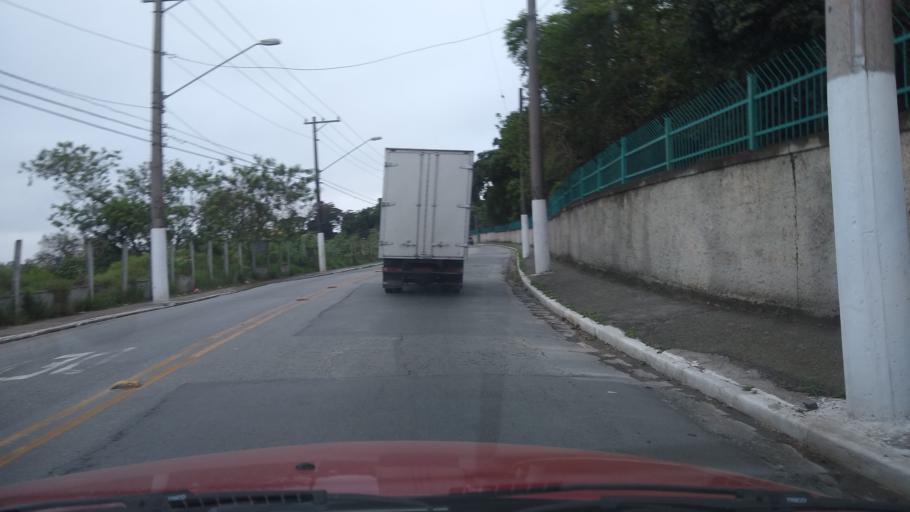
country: BR
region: Sao Paulo
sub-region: Diadema
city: Diadema
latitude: -23.6447
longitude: -46.6131
